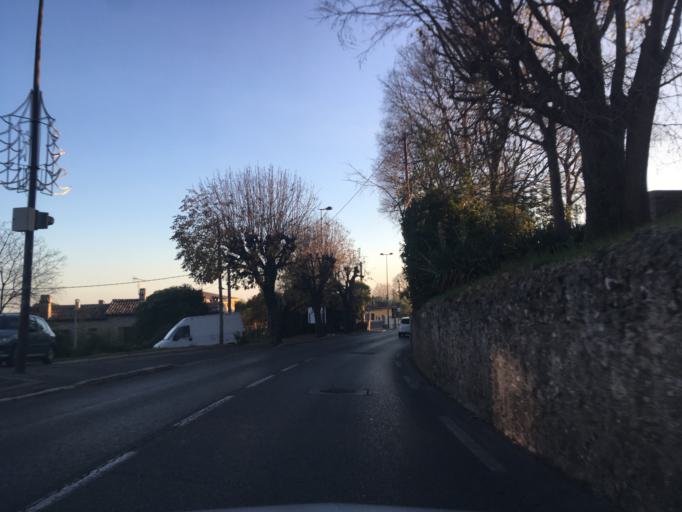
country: FR
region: Provence-Alpes-Cote d'Azur
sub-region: Departement des Alpes-Maritimes
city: Grasse
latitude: 43.6460
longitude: 6.9141
